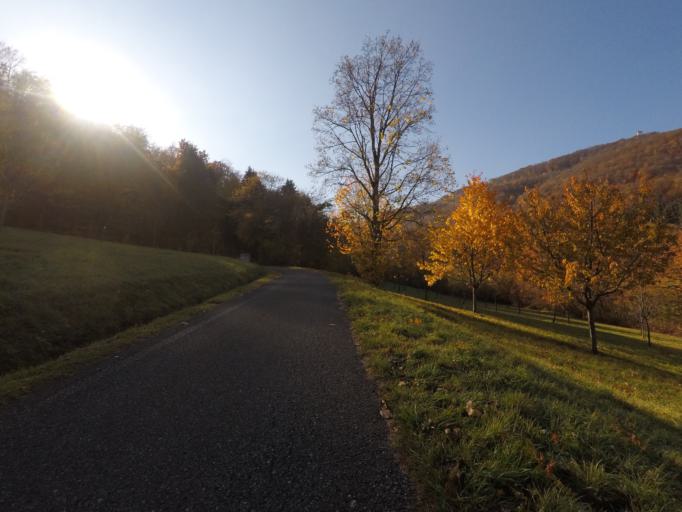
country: DE
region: Baden-Wuerttemberg
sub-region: Tuebingen Region
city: Pfullingen
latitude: 48.4429
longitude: 9.2397
